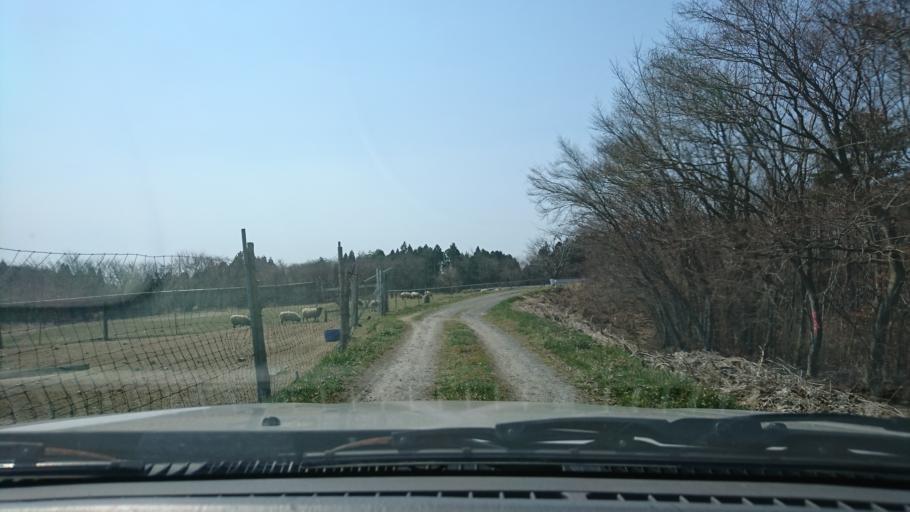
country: JP
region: Iwate
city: Ichinoseki
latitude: 38.8179
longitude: 141.2628
